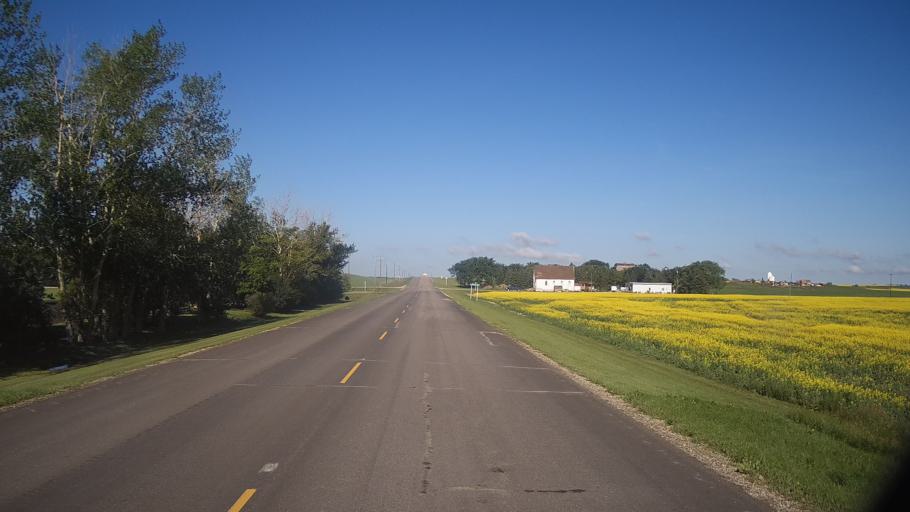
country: CA
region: Saskatchewan
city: Watrous
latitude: 51.6781
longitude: -105.4004
